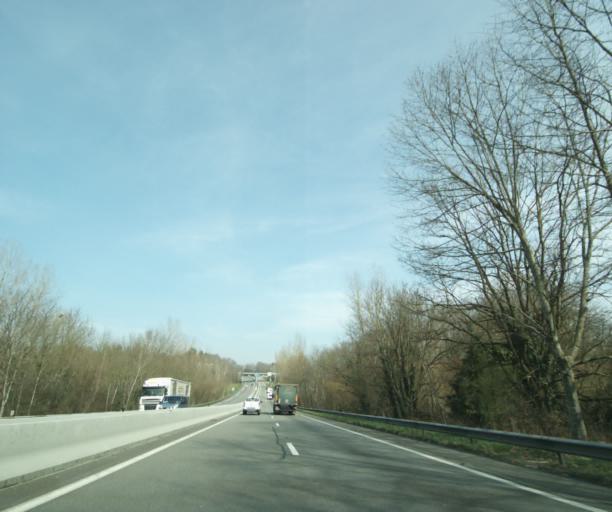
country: FR
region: Limousin
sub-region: Departement de la Haute-Vienne
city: Condat-sur-Vienne
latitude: 45.8038
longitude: 1.2971
